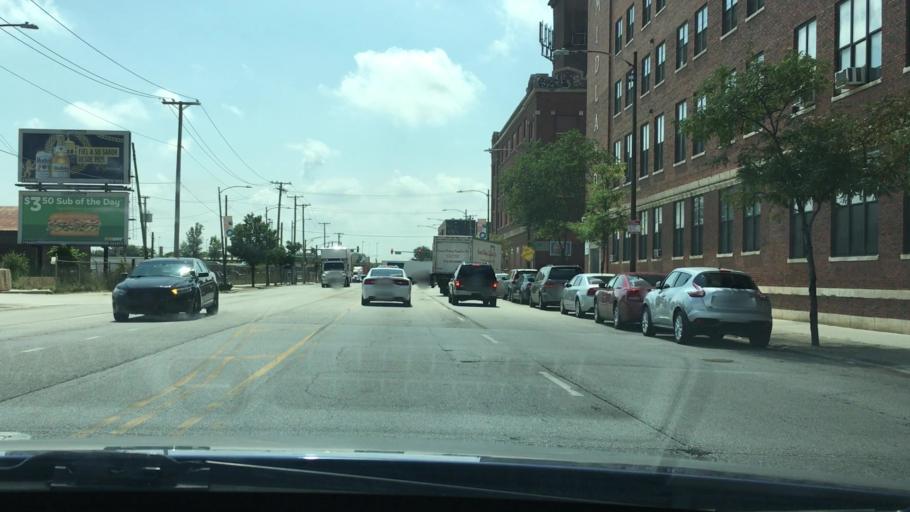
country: US
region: Illinois
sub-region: Cook County
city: Chicago
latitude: 41.8608
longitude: -87.6859
